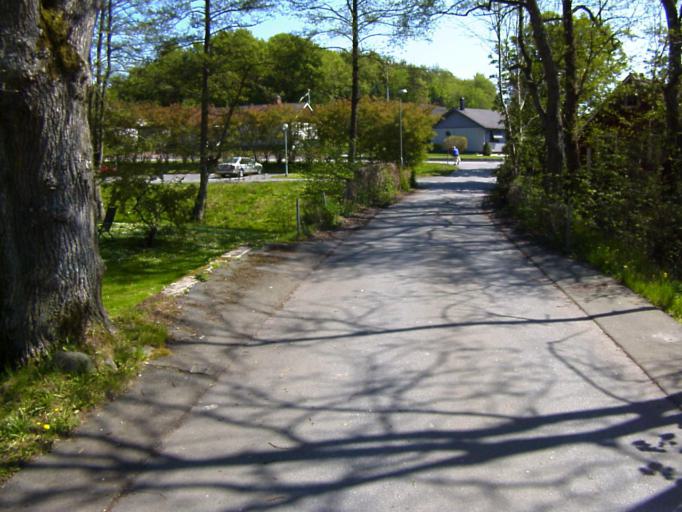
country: SE
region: Skane
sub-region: Kristianstads Kommun
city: Tollarp
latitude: 56.1747
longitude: 14.2885
